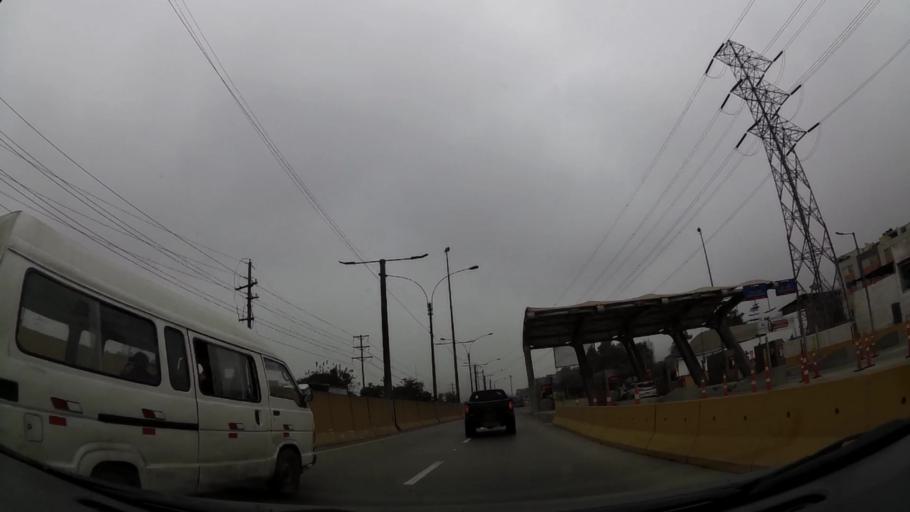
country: PE
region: Lima
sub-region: Lima
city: Urb. Santo Domingo
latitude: -11.9109
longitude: -77.0722
